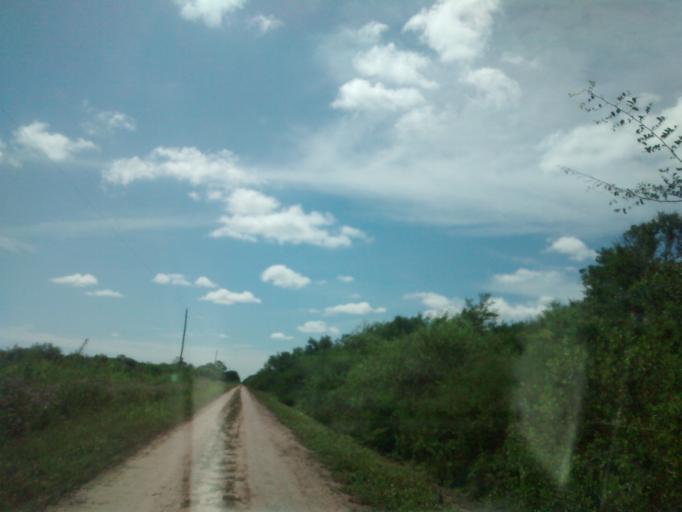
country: AR
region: Chaco
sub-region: Departamento de Quitilipi
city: Quitilipi
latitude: -26.7709
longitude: -60.2587
